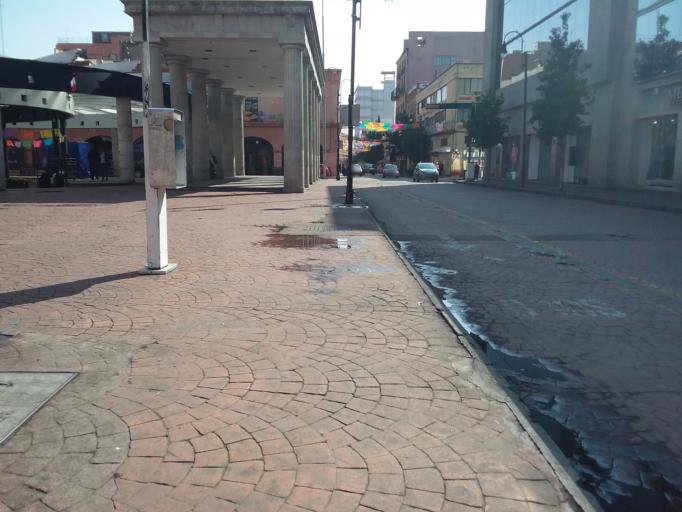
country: MX
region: Mexico
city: Toluca
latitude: 19.2903
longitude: -99.6582
